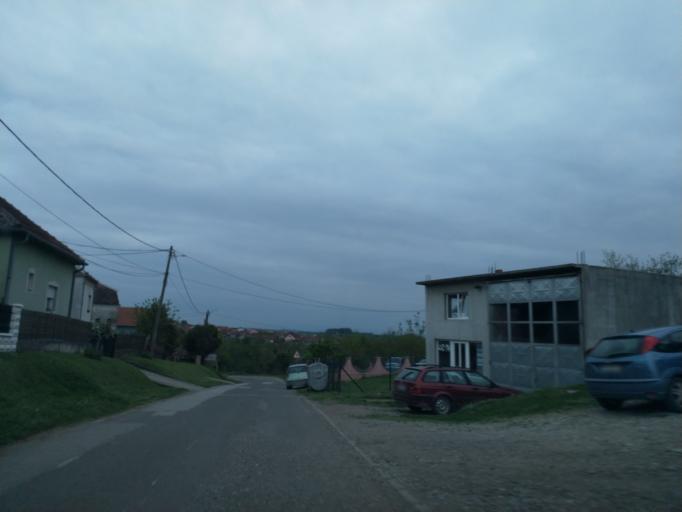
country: RS
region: Central Serbia
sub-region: Pomoravski Okrug
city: Paracin
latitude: 43.9461
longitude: 21.4926
